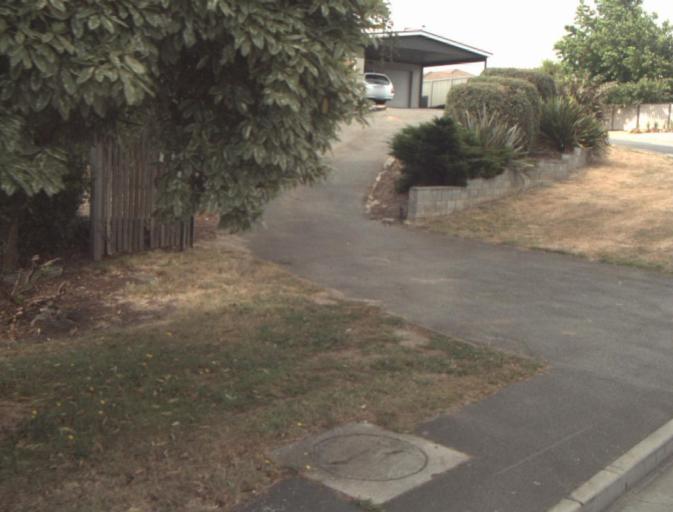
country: AU
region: Tasmania
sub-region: Launceston
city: Newstead
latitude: -41.4676
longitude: 147.1819
